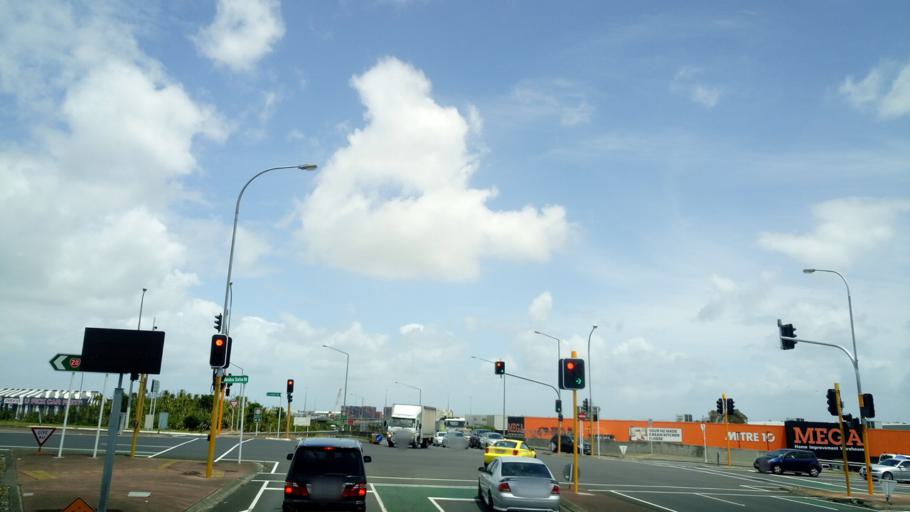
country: NZ
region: Auckland
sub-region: Auckland
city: Manukau City
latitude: -36.9951
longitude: 174.8748
